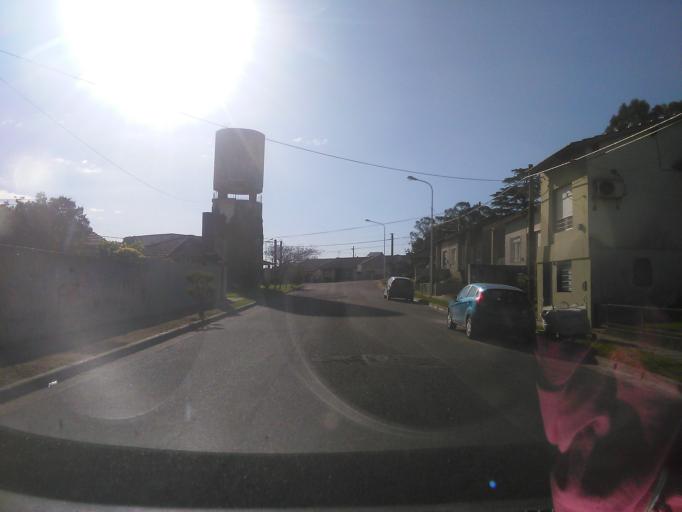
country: AR
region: Buenos Aires
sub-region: Partido de Tandil
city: Tandil
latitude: -37.3332
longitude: -59.1220
